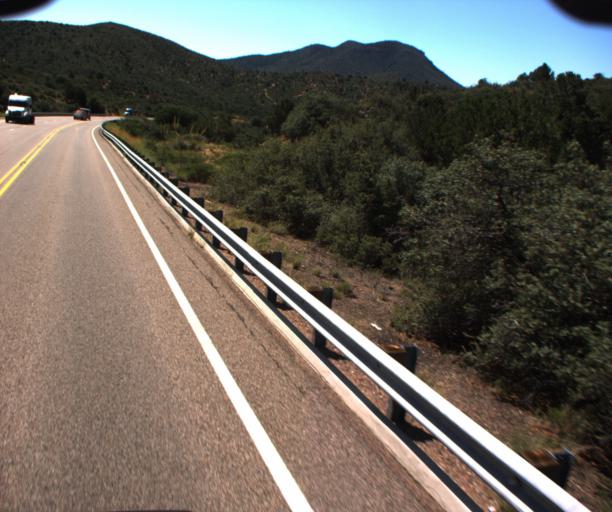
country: US
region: Arizona
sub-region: Gila County
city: Globe
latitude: 33.6340
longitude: -110.5840
